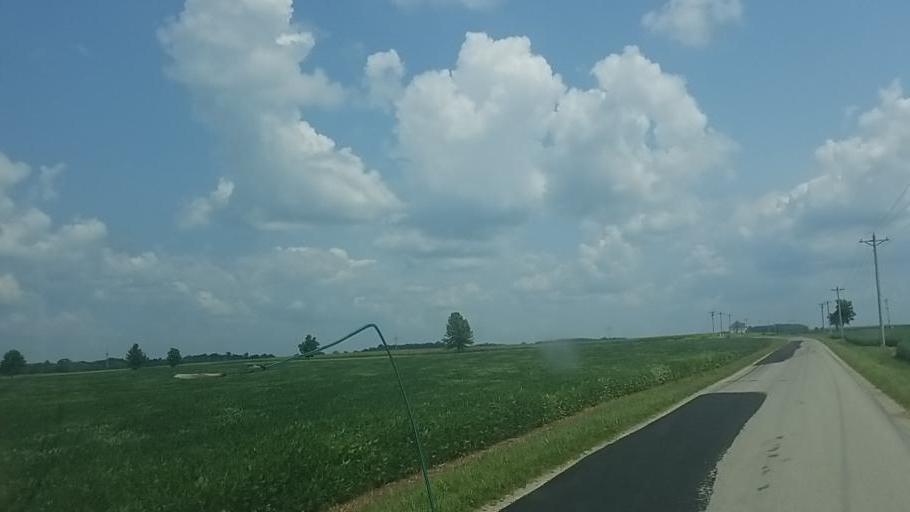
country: US
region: Ohio
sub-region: Wyandot County
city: Upper Sandusky
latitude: 40.9206
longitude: -83.1924
